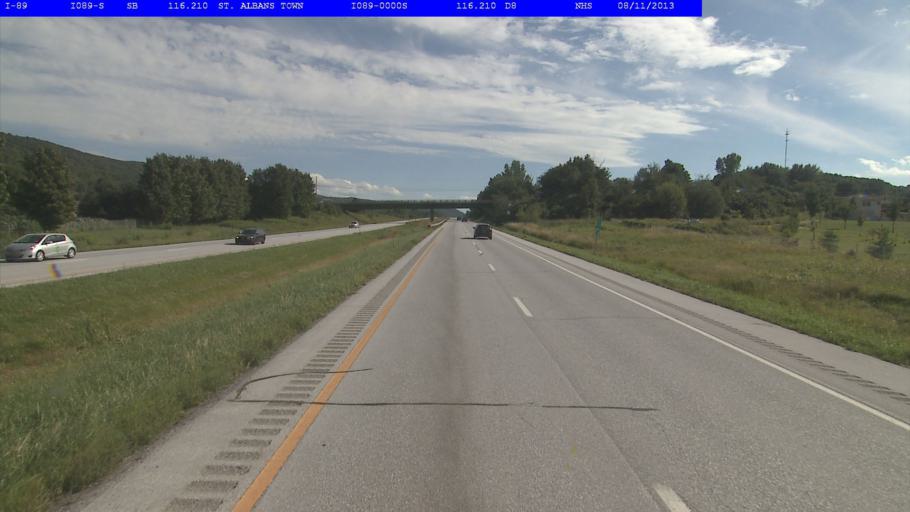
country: US
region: Vermont
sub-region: Franklin County
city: Saint Albans
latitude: 44.8298
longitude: -73.0619
